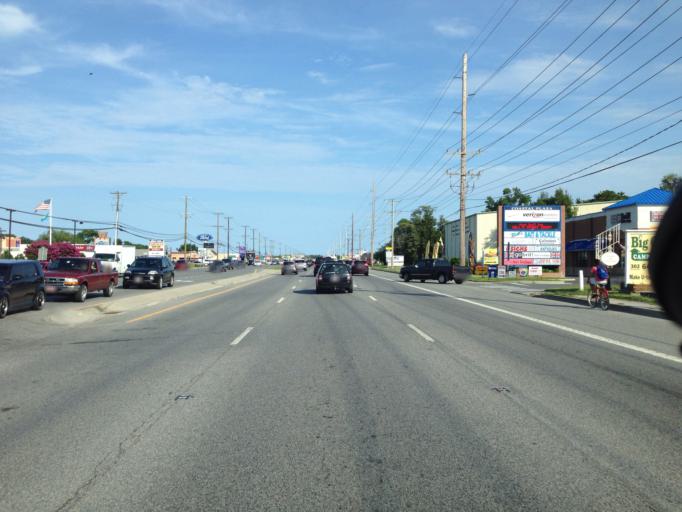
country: US
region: Delaware
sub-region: Sussex County
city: Lewes
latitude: 38.7407
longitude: -75.1473
